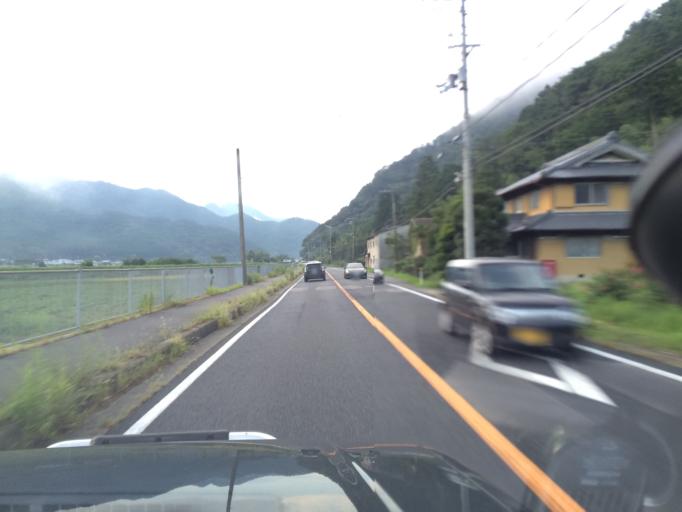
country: JP
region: Hyogo
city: Nishiwaki
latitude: 35.1243
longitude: 135.0078
